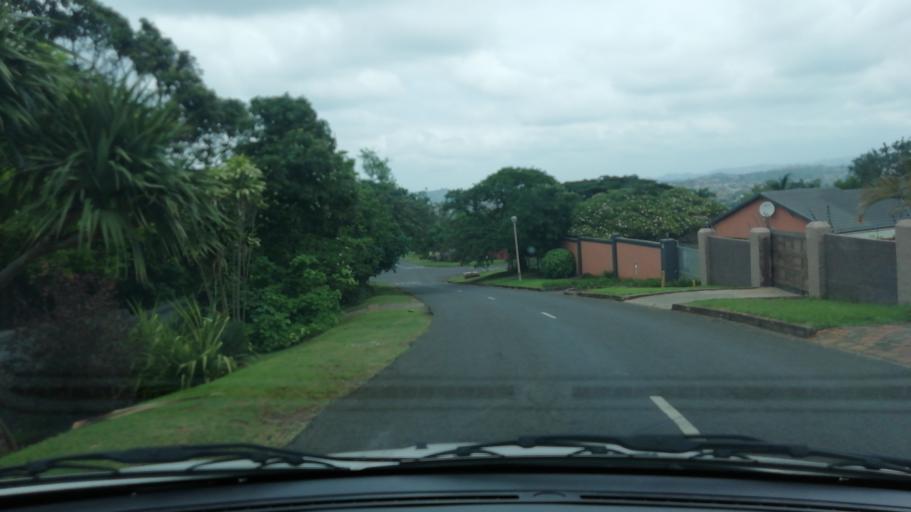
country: ZA
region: KwaZulu-Natal
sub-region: uThungulu District Municipality
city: Empangeni
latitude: -28.7569
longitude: 31.8879
